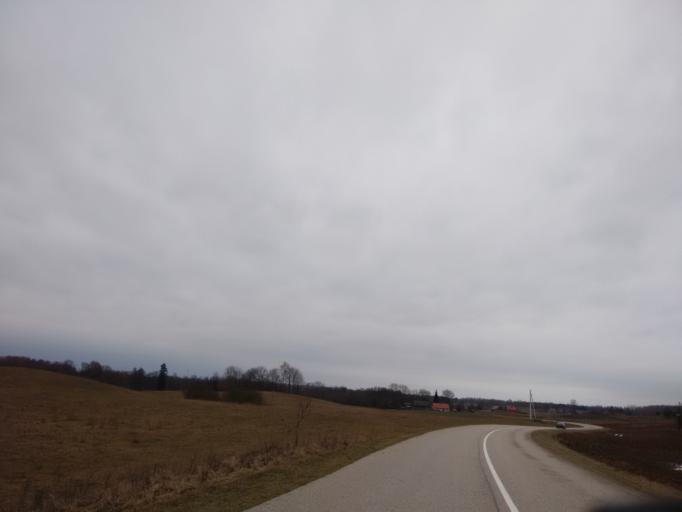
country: LT
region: Alytaus apskritis
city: Druskininkai
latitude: 54.2236
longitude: 23.8949
